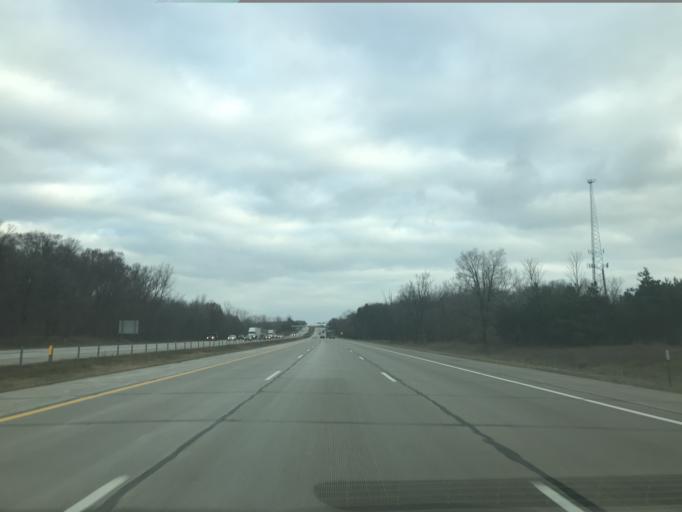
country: US
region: Michigan
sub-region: Eaton County
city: Waverly
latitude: 42.7617
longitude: -84.6676
